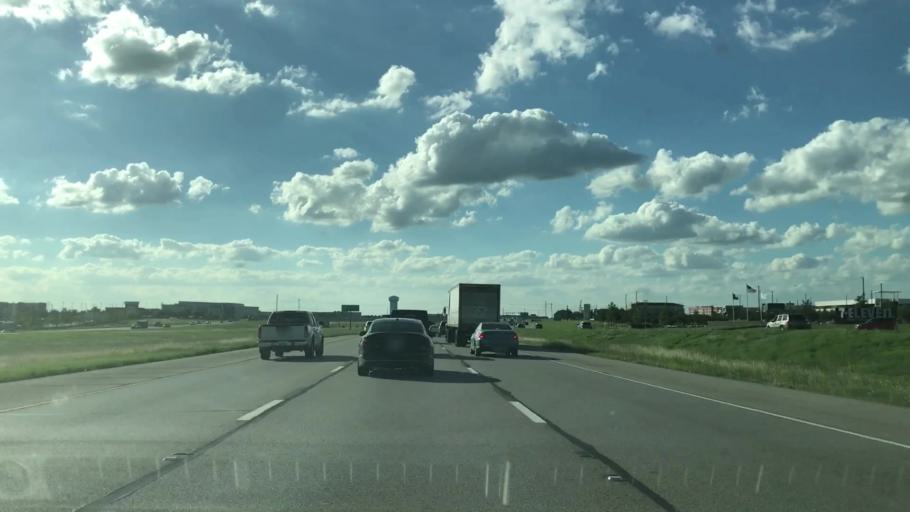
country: US
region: Texas
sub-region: Dallas County
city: Coppell
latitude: 32.9220
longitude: -96.9861
